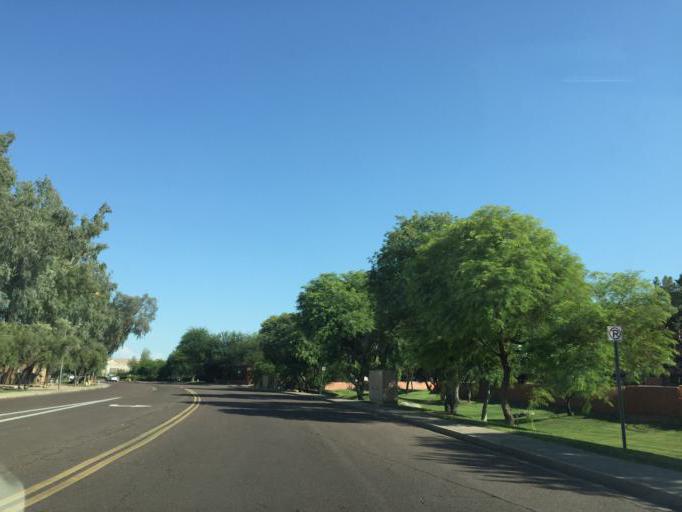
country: US
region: Arizona
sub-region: Maricopa County
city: Paradise Valley
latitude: 33.5980
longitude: -111.9872
